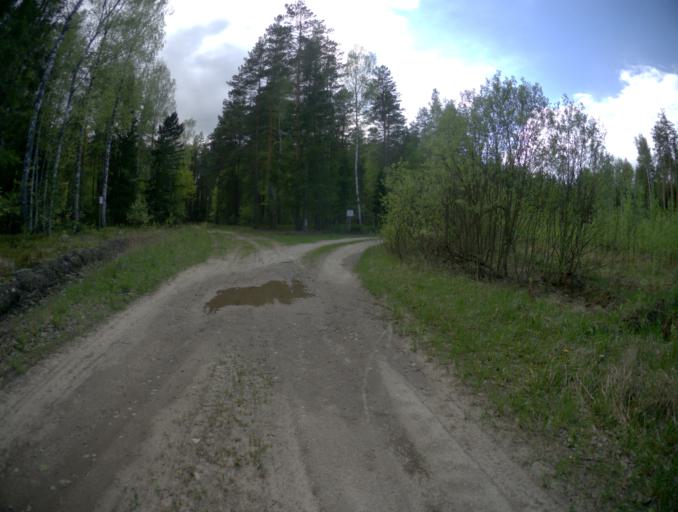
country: RU
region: Rjazan
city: Tuma
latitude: 55.2119
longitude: 40.4366
